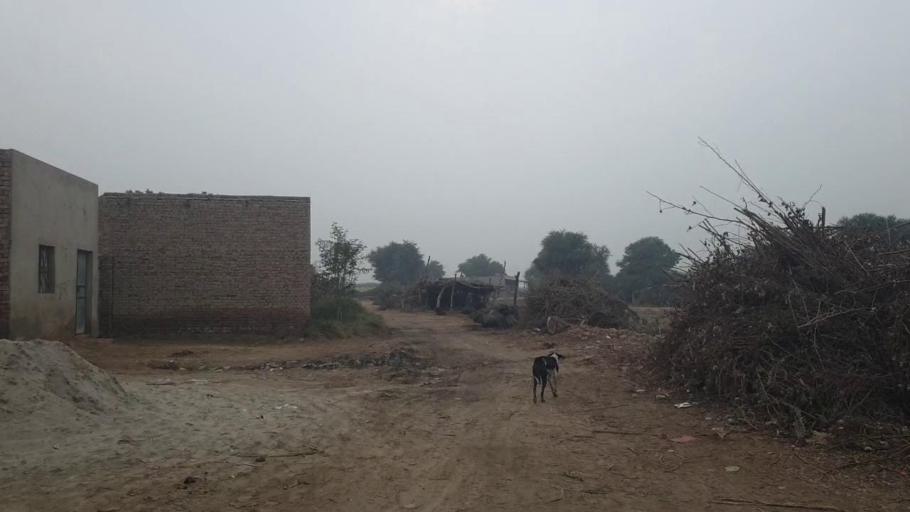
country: PK
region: Sindh
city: Tando Adam
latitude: 25.7040
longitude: 68.6187
